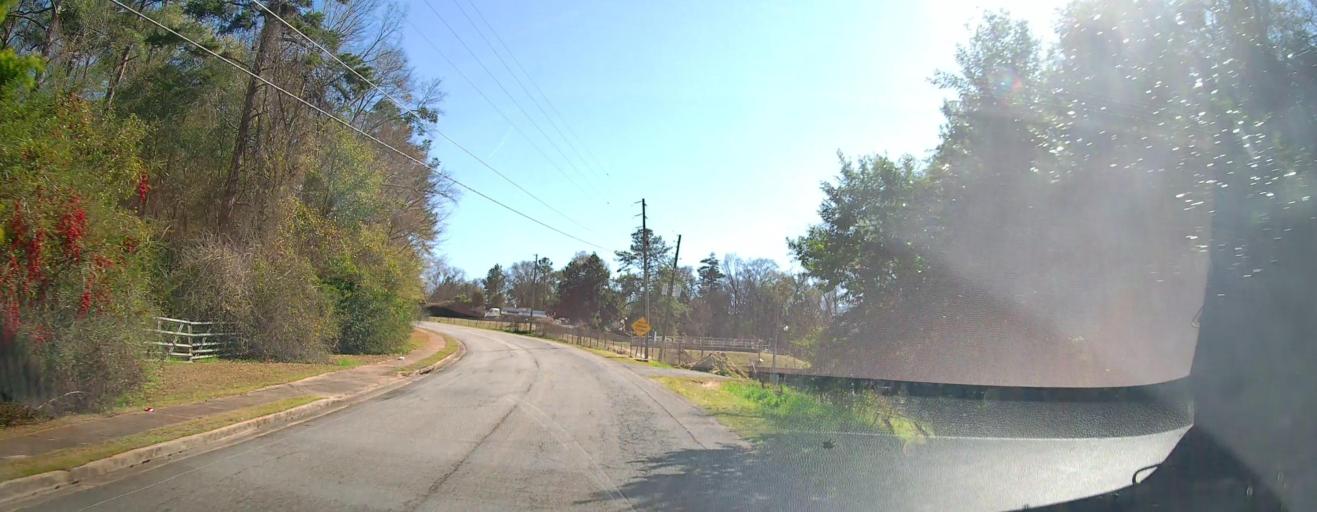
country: US
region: Georgia
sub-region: Macon County
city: Montezuma
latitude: 32.2846
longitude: -84.0312
